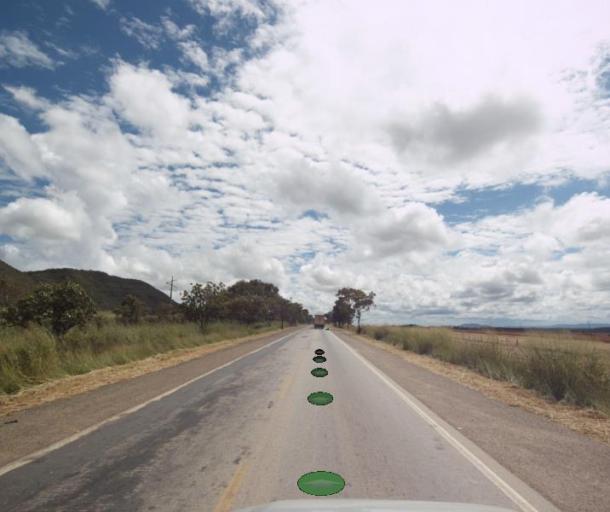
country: BR
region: Goias
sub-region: Uruacu
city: Uruacu
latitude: -14.4005
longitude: -49.1576
